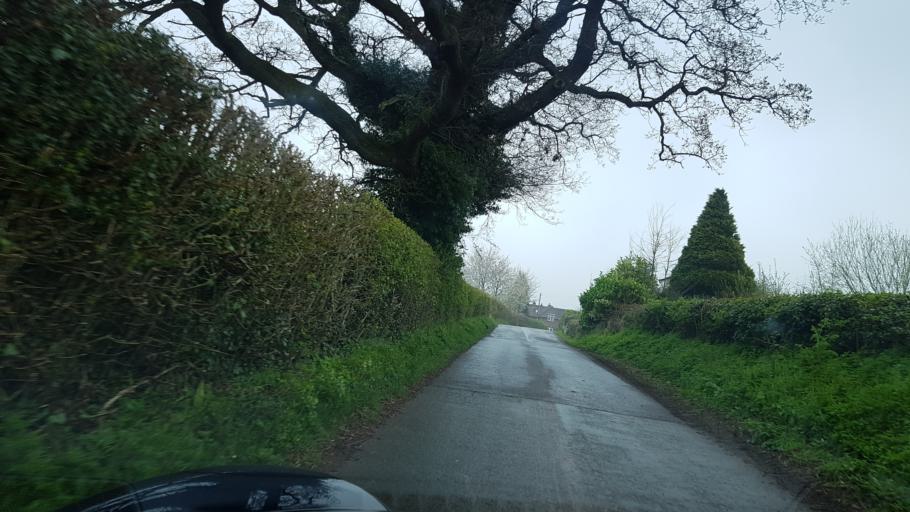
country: GB
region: England
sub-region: Herefordshire
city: Brockhampton
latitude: 51.9788
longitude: -2.6060
